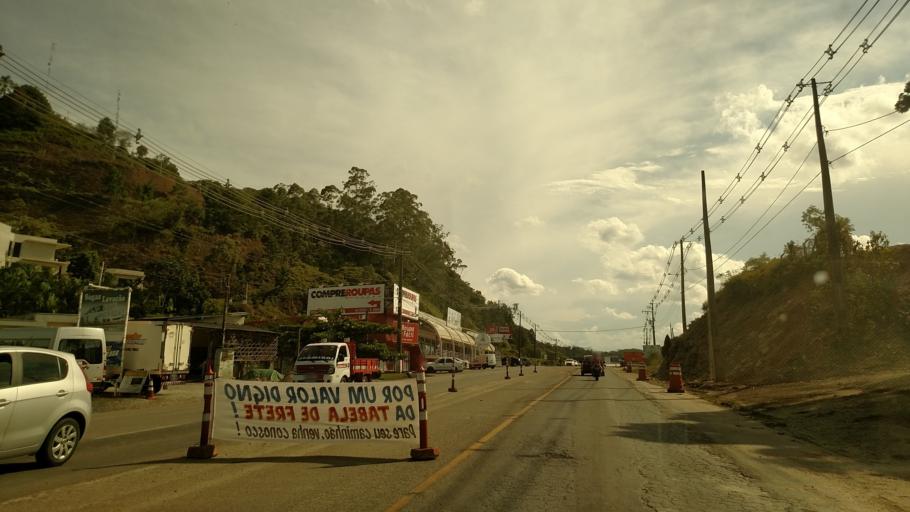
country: BR
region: Santa Catarina
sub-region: Itajai
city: Itajai
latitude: -26.9440
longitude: -48.7154
